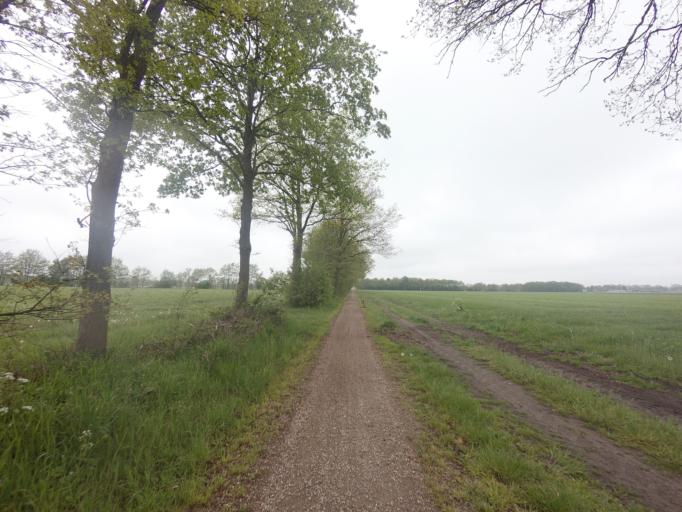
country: NL
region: Overijssel
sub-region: Gemeente Haaksbergen
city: Haaksbergen
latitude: 52.1295
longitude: 6.8125
